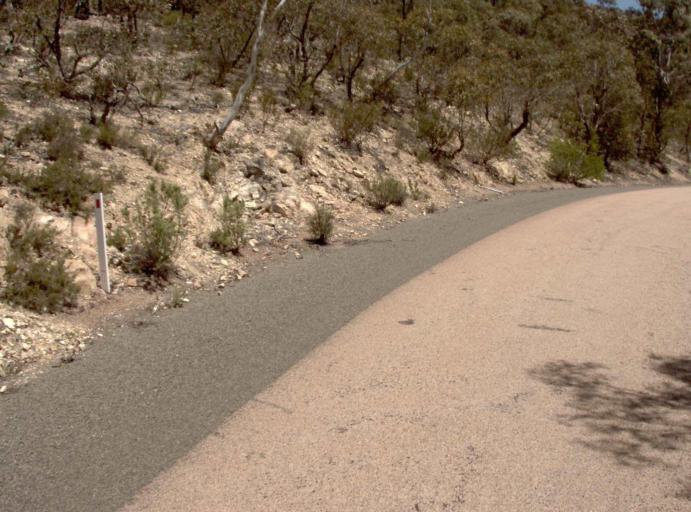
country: AU
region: New South Wales
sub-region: Snowy River
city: Jindabyne
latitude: -37.0689
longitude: 148.2934
